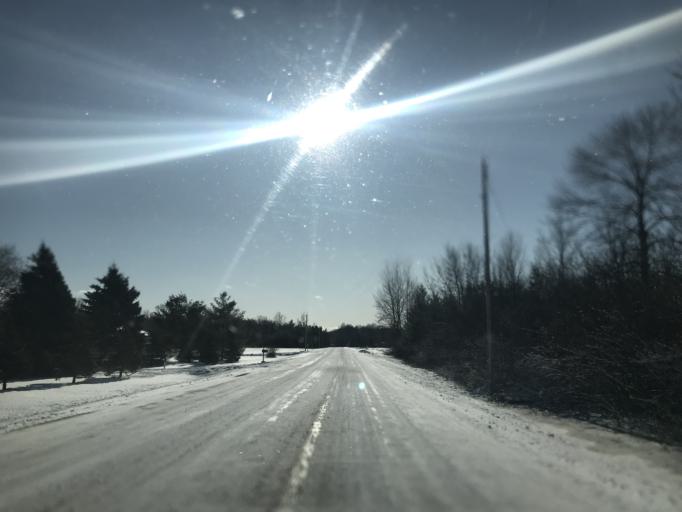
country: US
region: Wisconsin
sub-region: Door County
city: Sturgeon Bay
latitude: 44.8283
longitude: -87.5041
